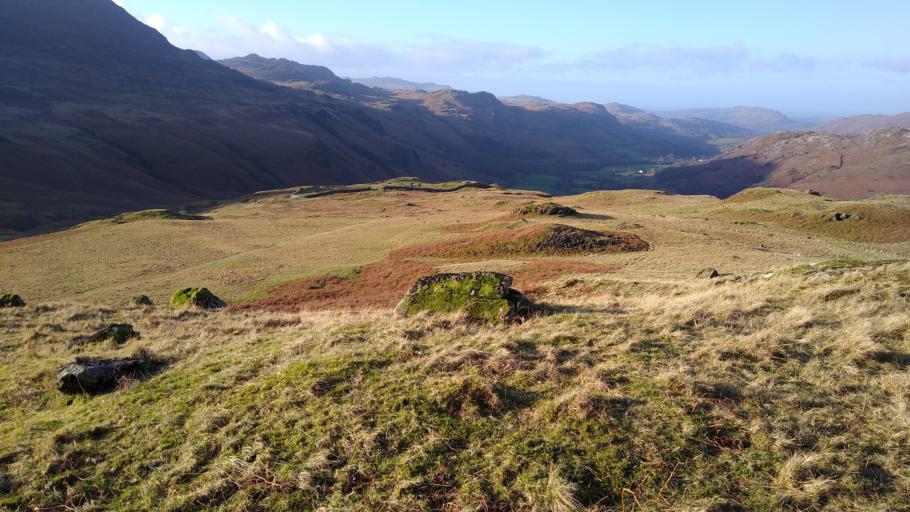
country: GB
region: England
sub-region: Cumbria
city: Keswick
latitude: 54.4056
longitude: -3.2004
